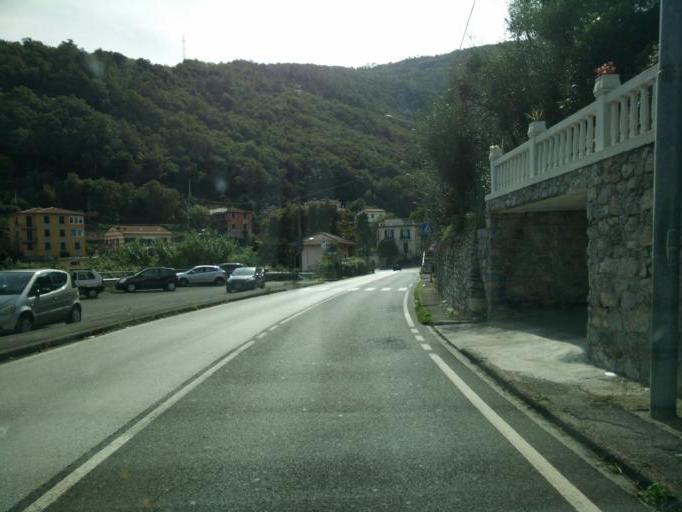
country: IT
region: Liguria
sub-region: Provincia di La Spezia
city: Le Grazie
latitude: 44.0806
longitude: 9.8216
